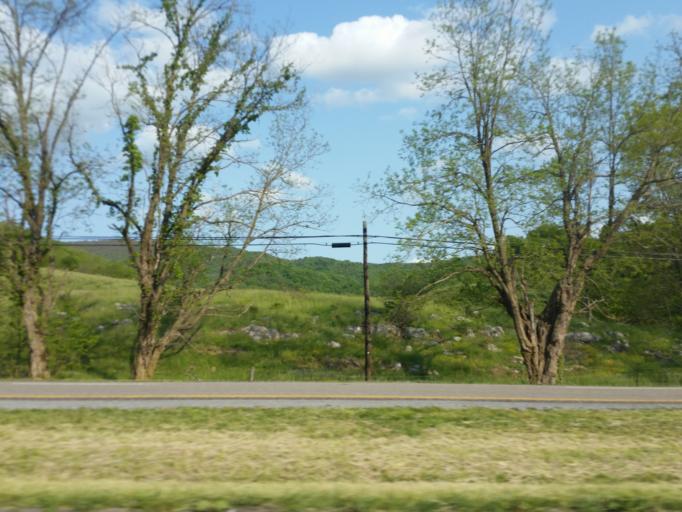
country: US
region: Virginia
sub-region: Tazewell County
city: Springville
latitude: 37.1609
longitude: -81.4643
